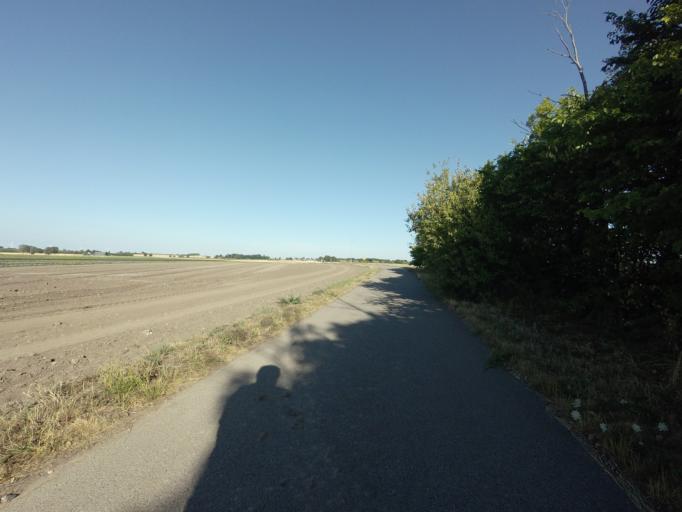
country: SE
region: Skane
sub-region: Trelleborgs Kommun
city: Skare
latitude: 55.4001
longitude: 13.0942
